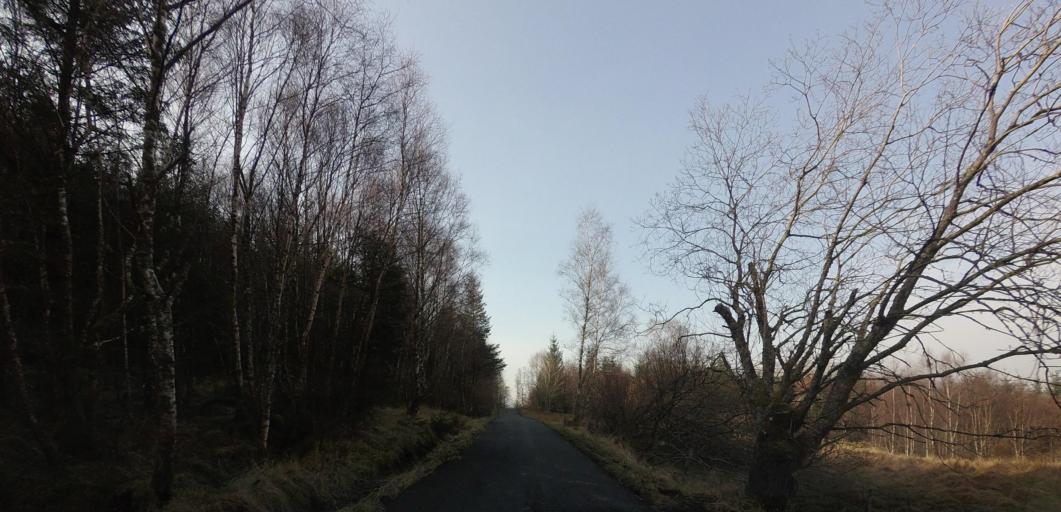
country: GB
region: Scotland
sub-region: Stirling
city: Callander
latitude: 56.4674
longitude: -4.2874
